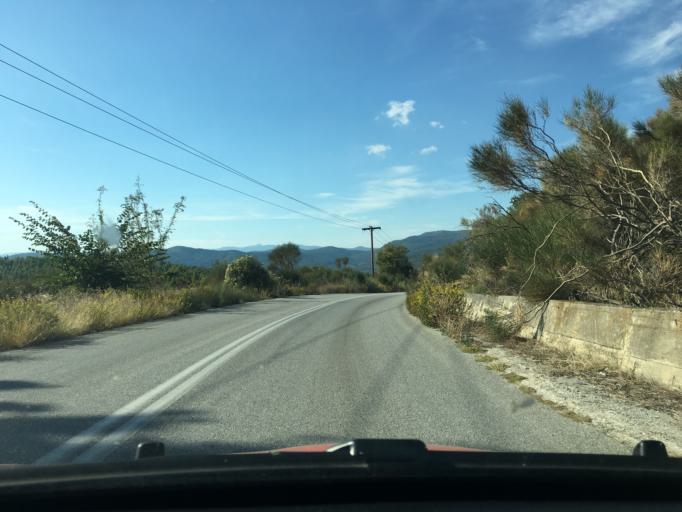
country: GR
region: Central Macedonia
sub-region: Nomos Chalkidikis
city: Ierissos
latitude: 40.3871
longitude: 23.8157
